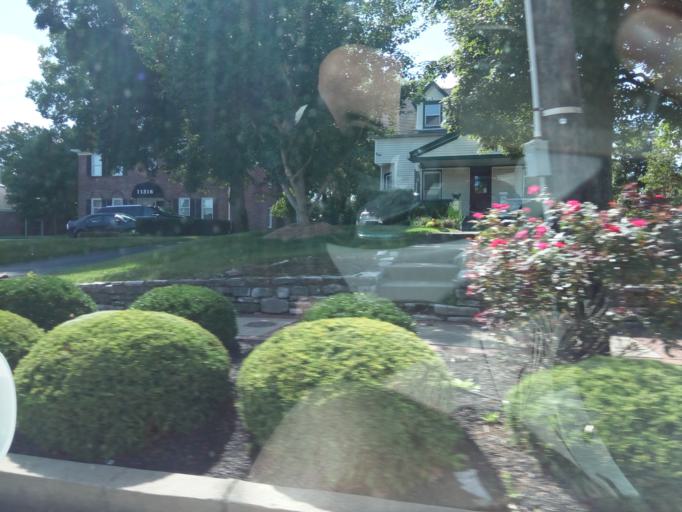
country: US
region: Kentucky
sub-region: Jefferson County
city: Middletown
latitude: 38.2446
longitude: -85.5424
